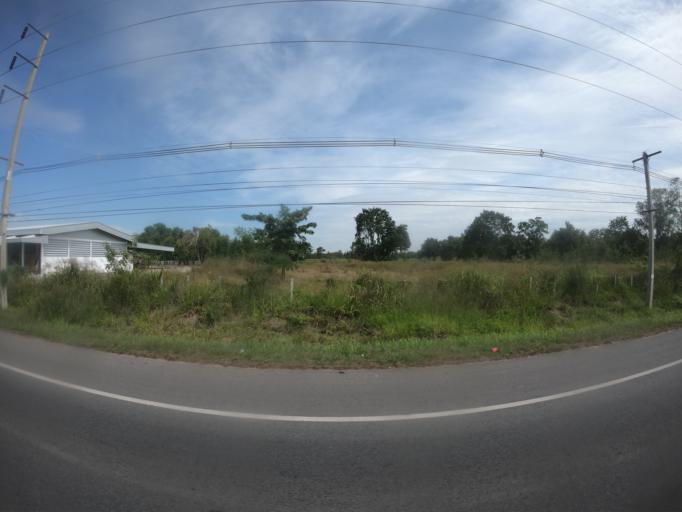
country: TH
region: Maha Sarakham
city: Chiang Yuen
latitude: 16.4369
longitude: 103.0508
